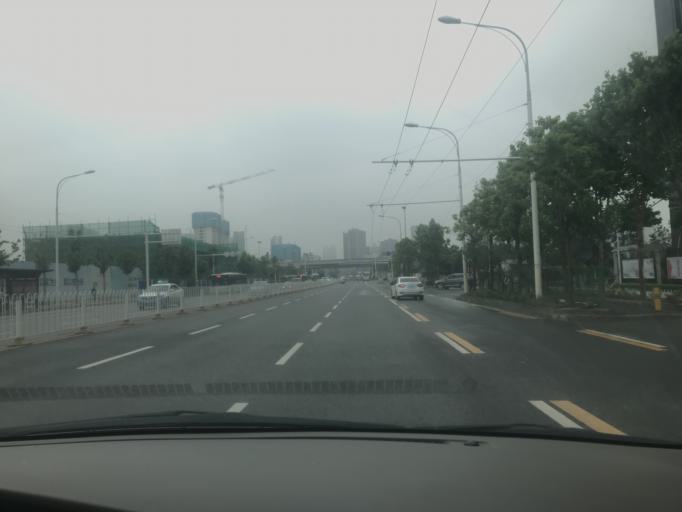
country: CN
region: Hubei
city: Yongfeng
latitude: 30.5568
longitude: 114.2345
